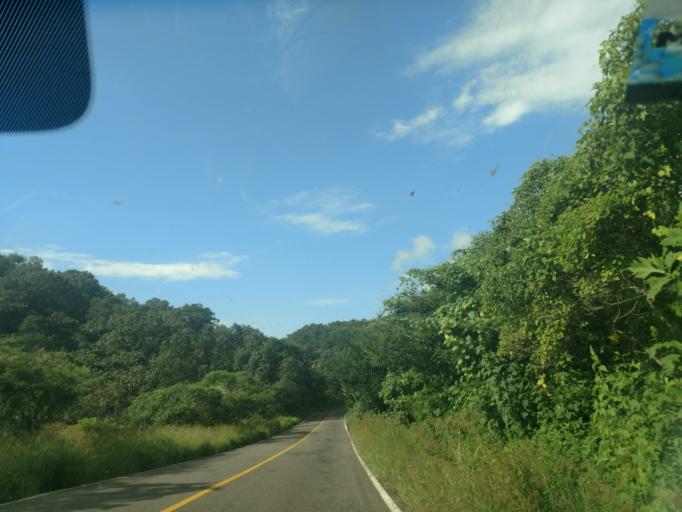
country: MX
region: Jalisco
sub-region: Atengo
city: Soyatlan del Oro
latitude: 20.4931
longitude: -104.3598
